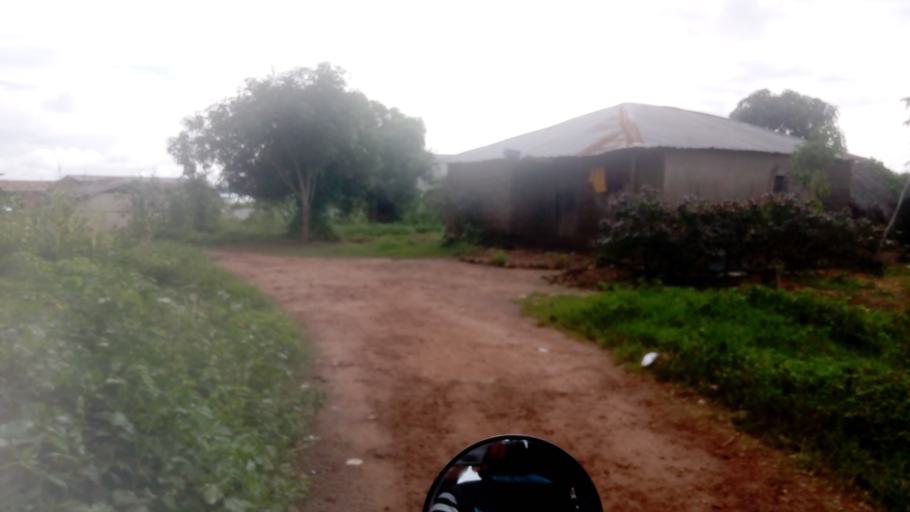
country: SL
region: Northern Province
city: Port Loko
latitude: 8.7083
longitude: -12.6833
